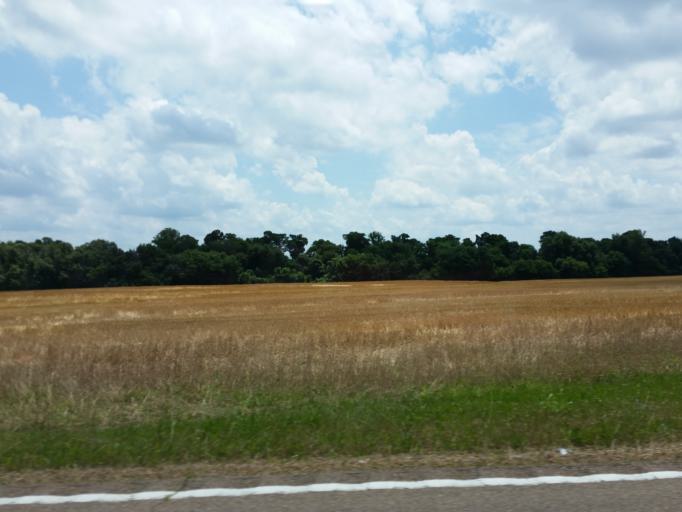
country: US
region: Tennessee
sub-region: Lake County
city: Tiptonville
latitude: 36.4072
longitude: -89.4477
